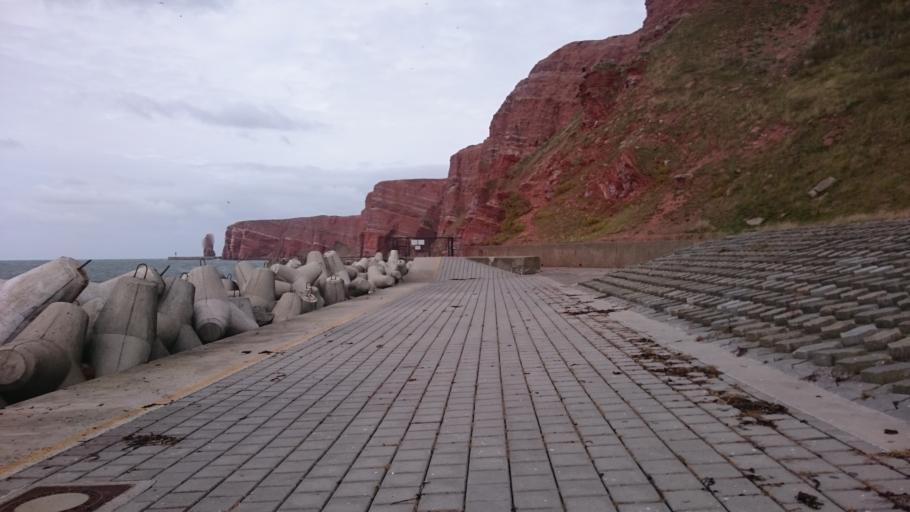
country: DE
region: Schleswig-Holstein
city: Helgoland
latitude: 54.1792
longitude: 7.8823
